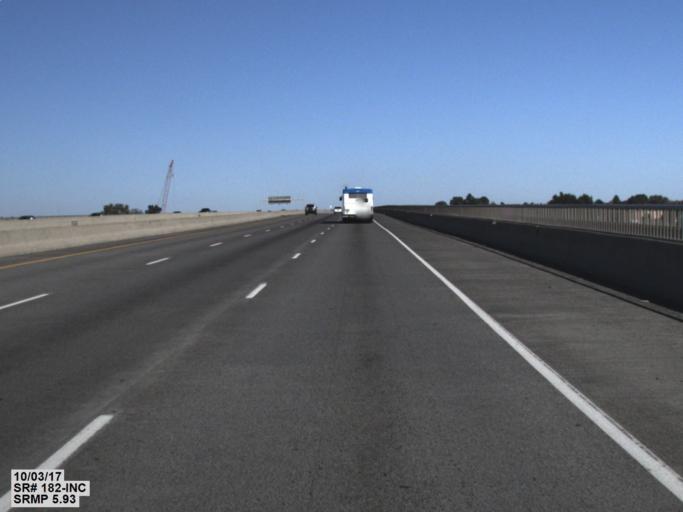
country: US
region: Washington
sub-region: Benton County
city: Richland
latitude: 46.2633
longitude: -119.2444
